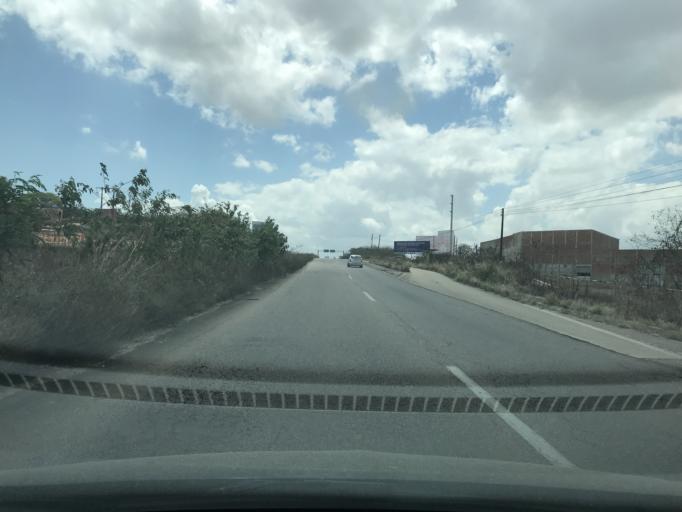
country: BR
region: Pernambuco
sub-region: Caruaru
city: Caruaru
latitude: -8.3080
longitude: -35.9556
